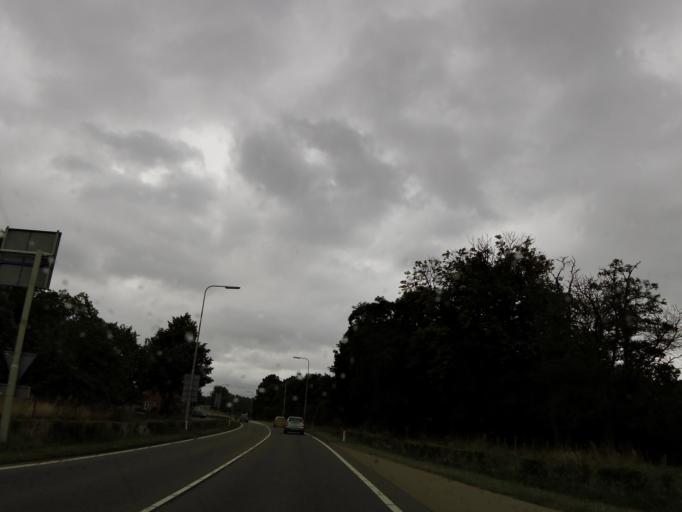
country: BE
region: Flanders
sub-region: Provincie Limburg
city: Maaseik
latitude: 51.0813
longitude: 5.8147
